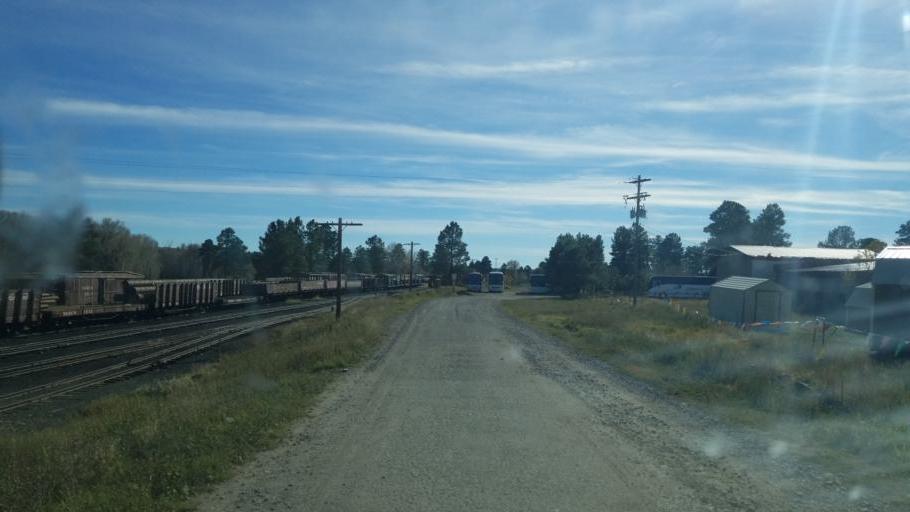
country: US
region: New Mexico
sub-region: Rio Arriba County
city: Chama
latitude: 36.9010
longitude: -106.5795
